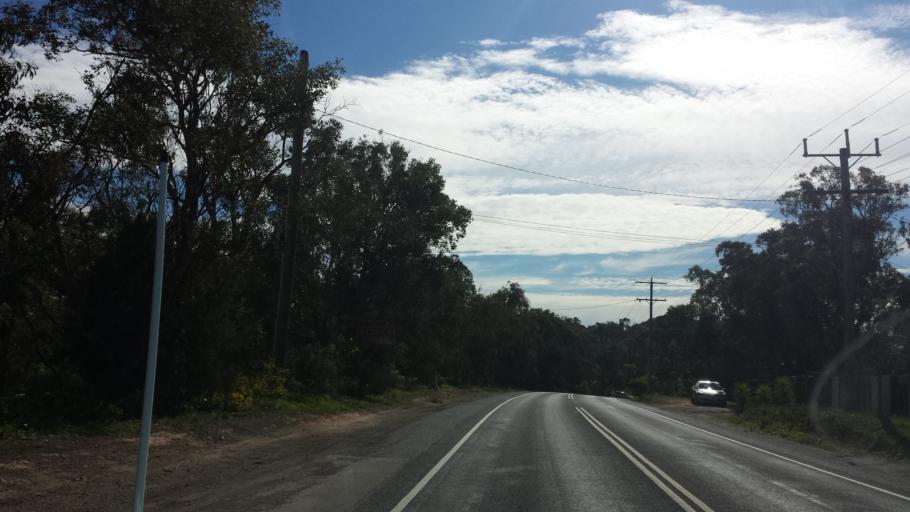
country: AU
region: Victoria
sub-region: Nillumbik
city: North Warrandyte
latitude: -37.7224
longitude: 145.2263
